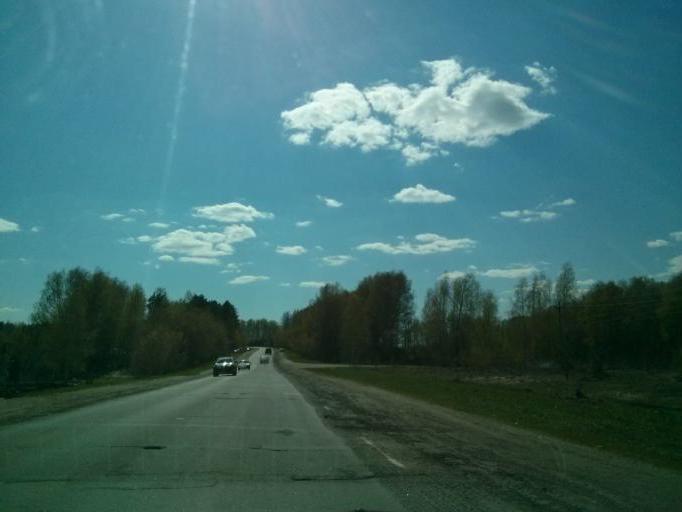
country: RU
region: Nizjnij Novgorod
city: Taremskoye
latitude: 55.9169
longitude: 43.0270
